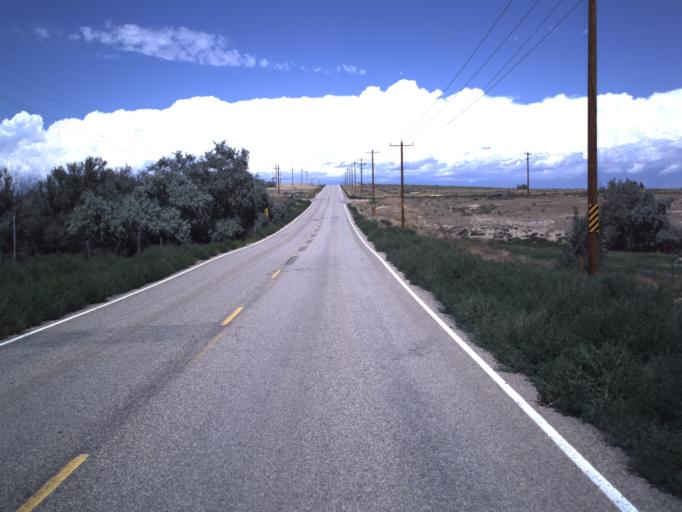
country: US
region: Utah
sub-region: Uintah County
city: Naples
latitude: 40.1496
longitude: -109.6641
